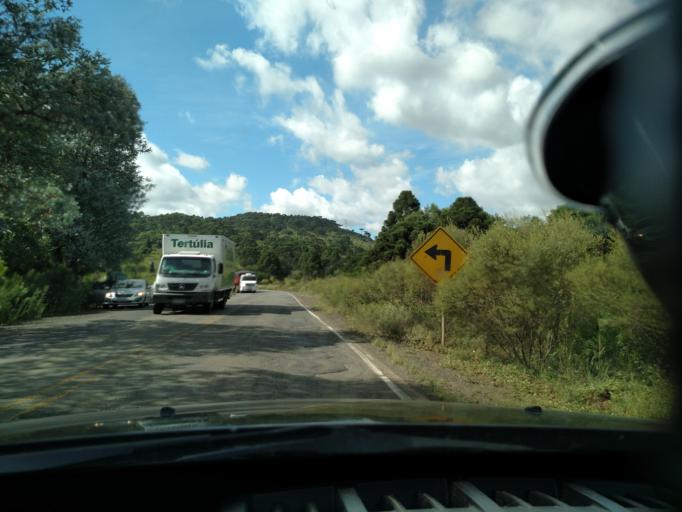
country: BR
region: Santa Catarina
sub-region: Sao Joaquim
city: Sao Joaquim
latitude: -28.0905
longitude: -50.0611
